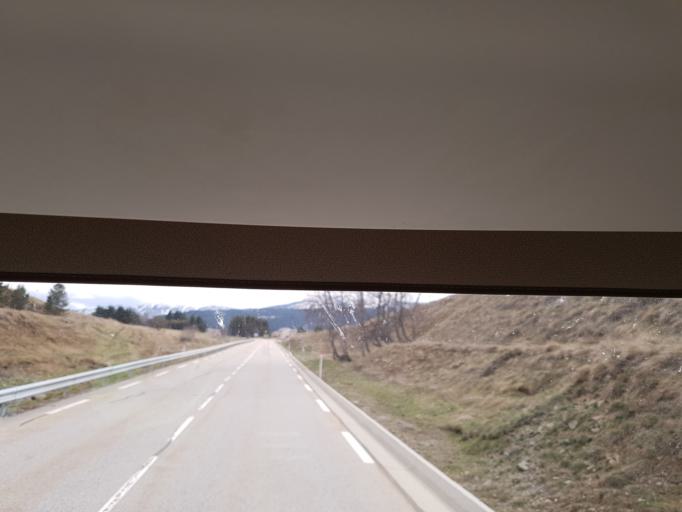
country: ES
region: Catalonia
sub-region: Provincia de Girona
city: Llivia
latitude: 42.6499
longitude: 2.1196
